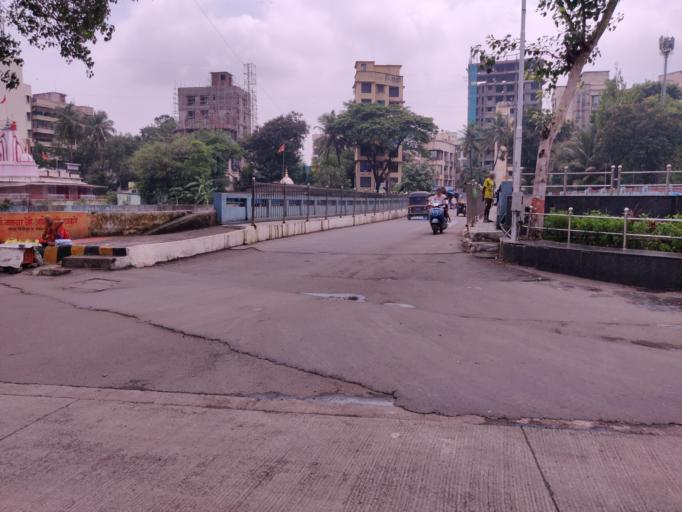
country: IN
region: Maharashtra
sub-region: Mumbai Suburban
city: Borivli
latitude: 19.2551
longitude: 72.8561
